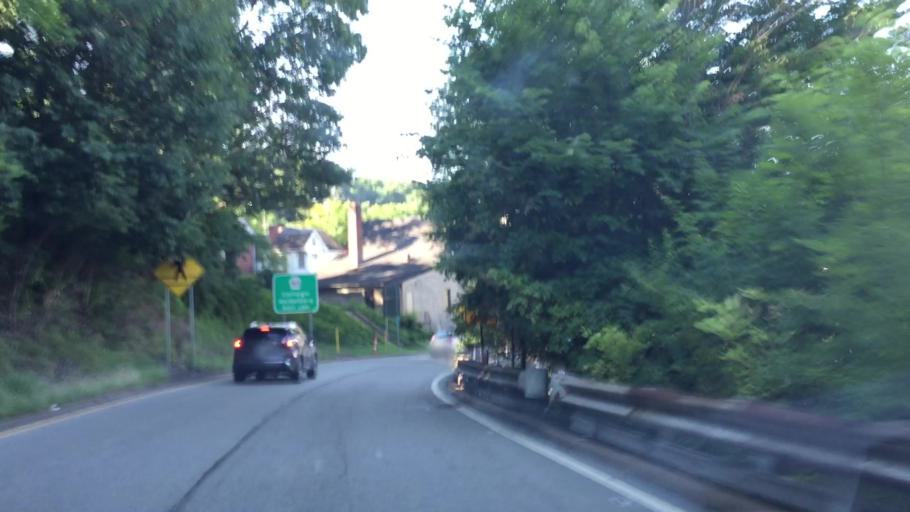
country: US
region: Pennsylvania
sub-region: Allegheny County
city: Carnegie
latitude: 40.4108
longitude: -80.0801
